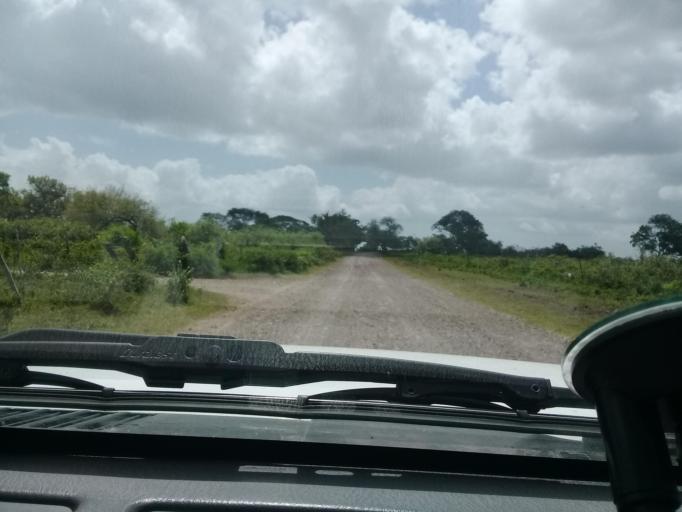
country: MX
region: Veracruz
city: Moralillo
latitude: 22.1595
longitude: -97.9927
